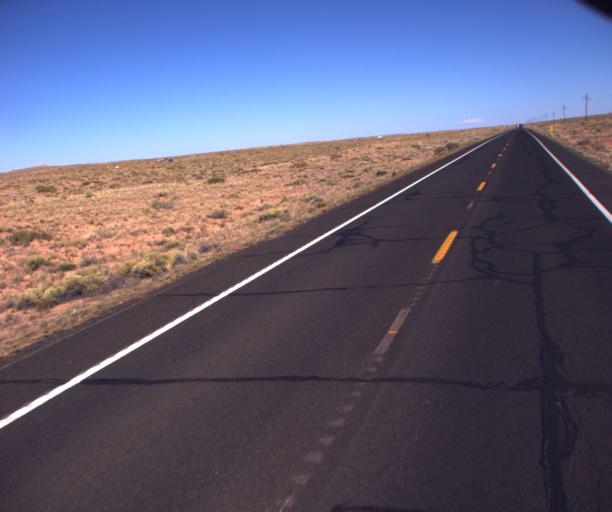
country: US
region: Arizona
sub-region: Coconino County
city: Tuba City
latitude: 36.1332
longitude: -111.1818
